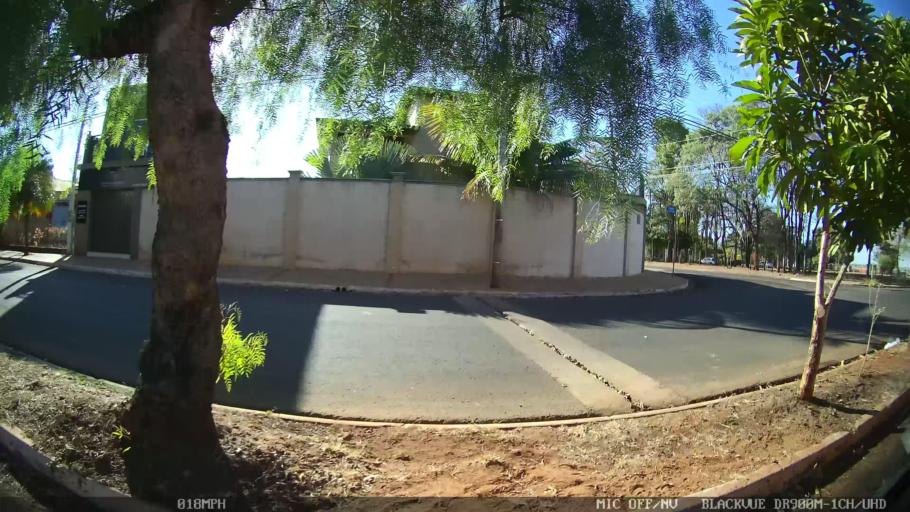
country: BR
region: Sao Paulo
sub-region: Olimpia
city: Olimpia
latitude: -20.7252
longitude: -48.8951
